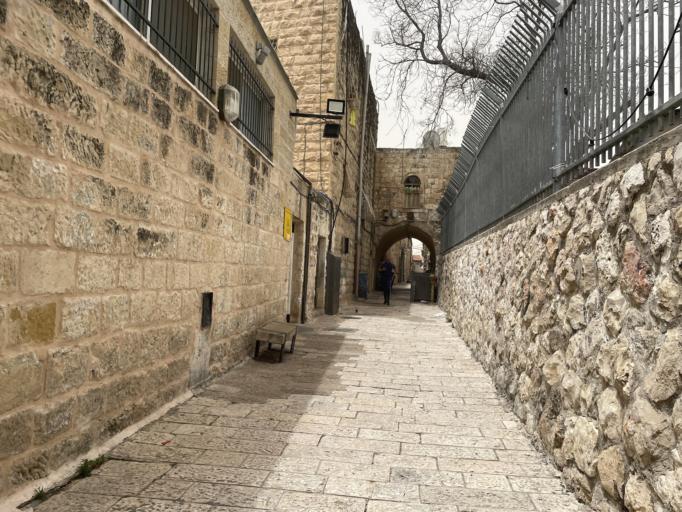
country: PS
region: West Bank
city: East Jerusalem
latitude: 31.7822
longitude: 35.2324
